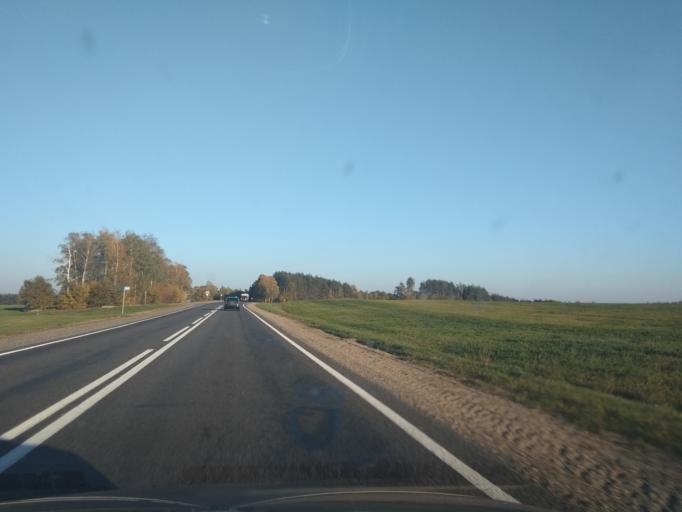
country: BY
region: Grodnenskaya
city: Zel'va
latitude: 53.1407
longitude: 24.7004
